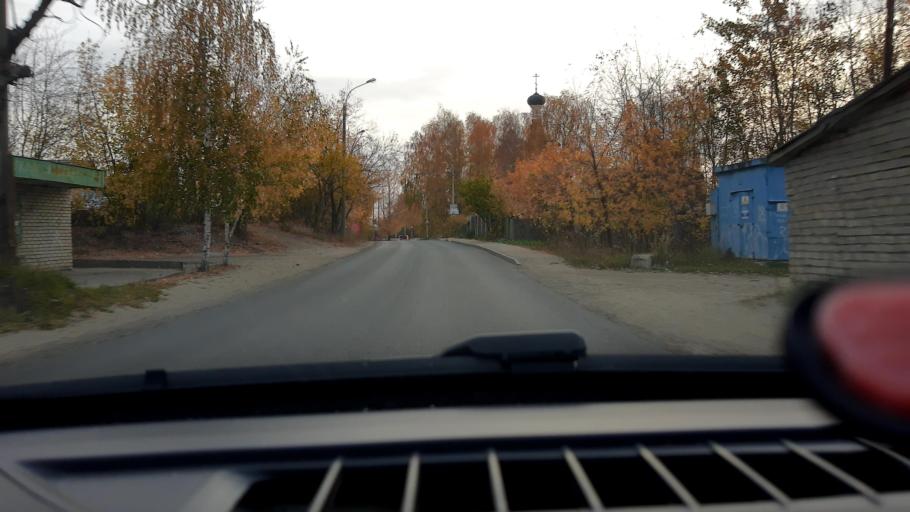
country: RU
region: Nizjnij Novgorod
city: Gorbatovka
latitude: 56.3310
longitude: 43.8206
